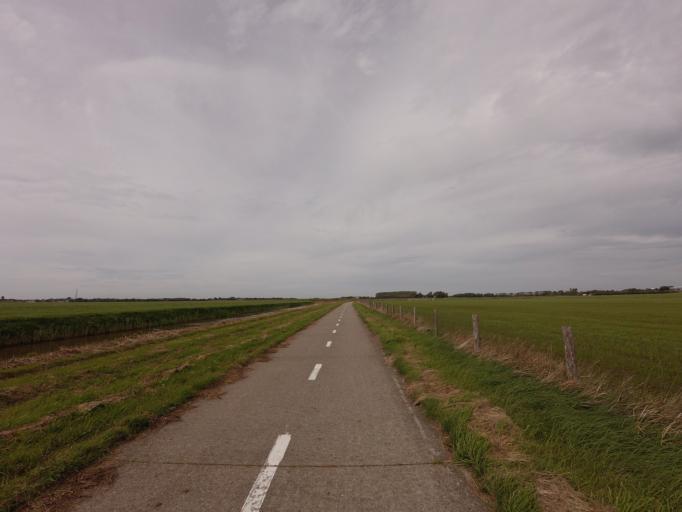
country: NL
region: North Holland
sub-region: Gemeente Texel
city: Den Burg
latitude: 53.0608
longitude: 4.8269
